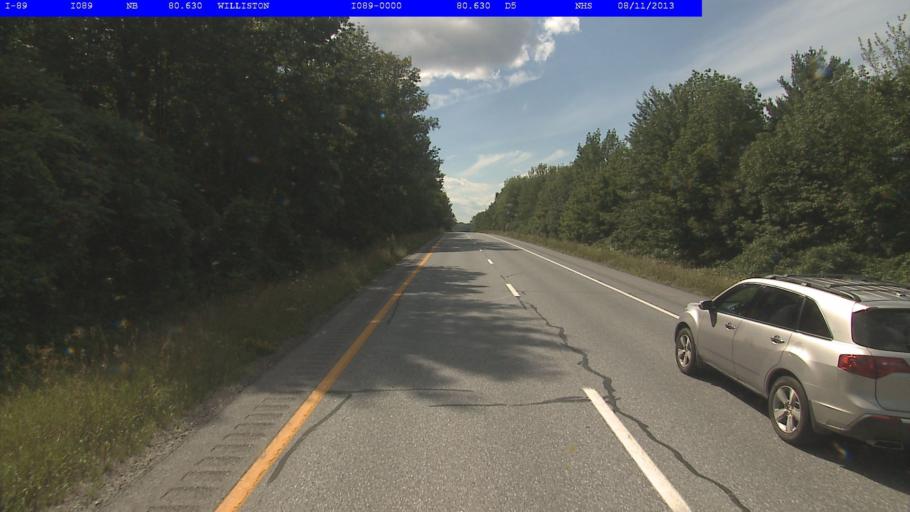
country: US
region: Vermont
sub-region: Chittenden County
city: Williston
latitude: 44.4333
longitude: -73.0484
